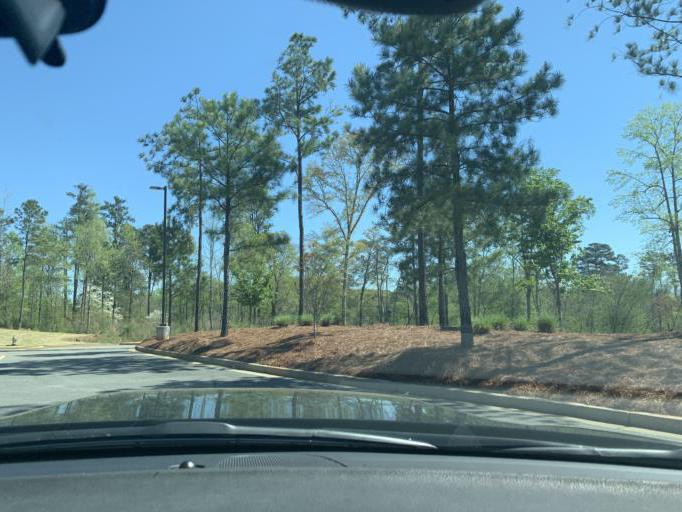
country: US
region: Georgia
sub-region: Fulton County
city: Milton
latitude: 34.1253
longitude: -84.2082
